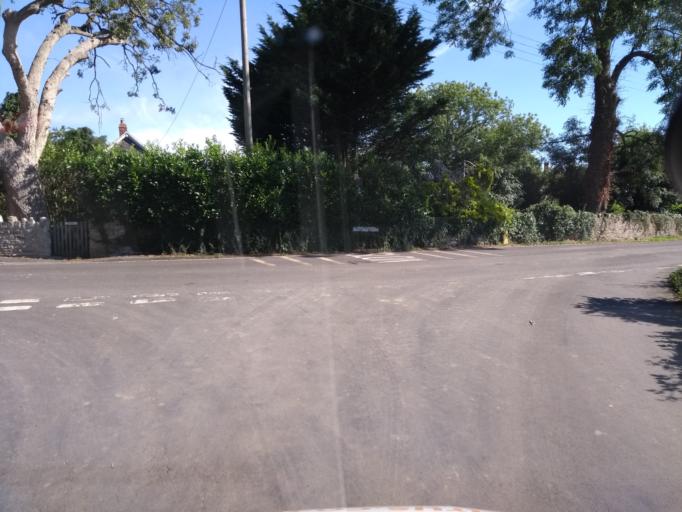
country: GB
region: England
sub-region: Somerset
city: Glastonbury
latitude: 51.1118
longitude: -2.6370
